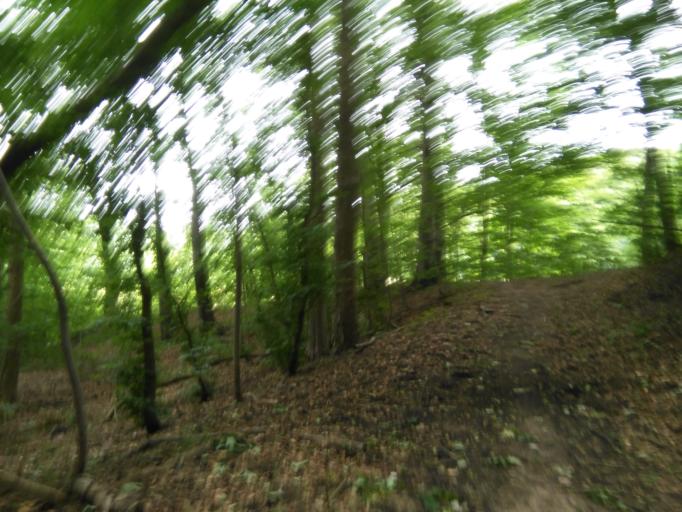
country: DK
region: Central Jutland
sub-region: Arhus Kommune
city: Beder
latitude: 56.0692
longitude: 10.2078
